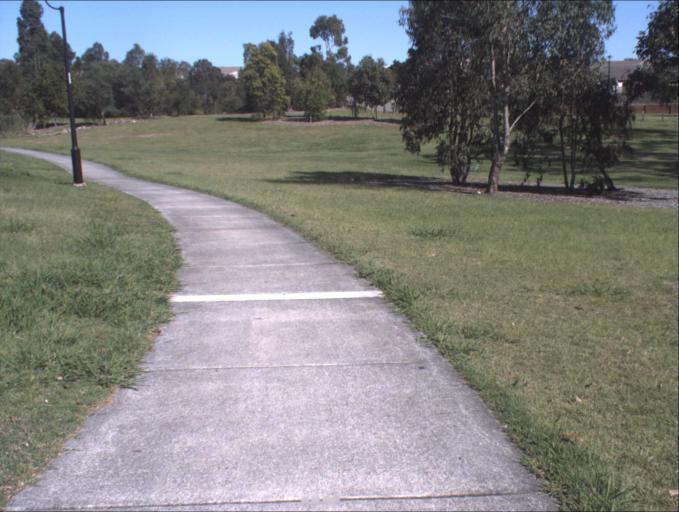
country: AU
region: Queensland
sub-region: Logan
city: Windaroo
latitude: -27.7216
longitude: 153.1721
